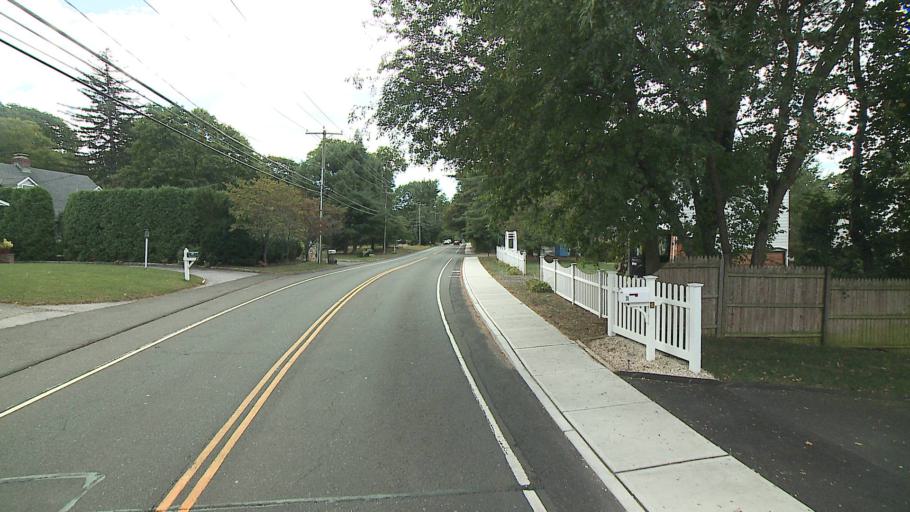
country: US
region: Connecticut
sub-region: Fairfield County
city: Stamford
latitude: 41.0828
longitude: -73.5115
